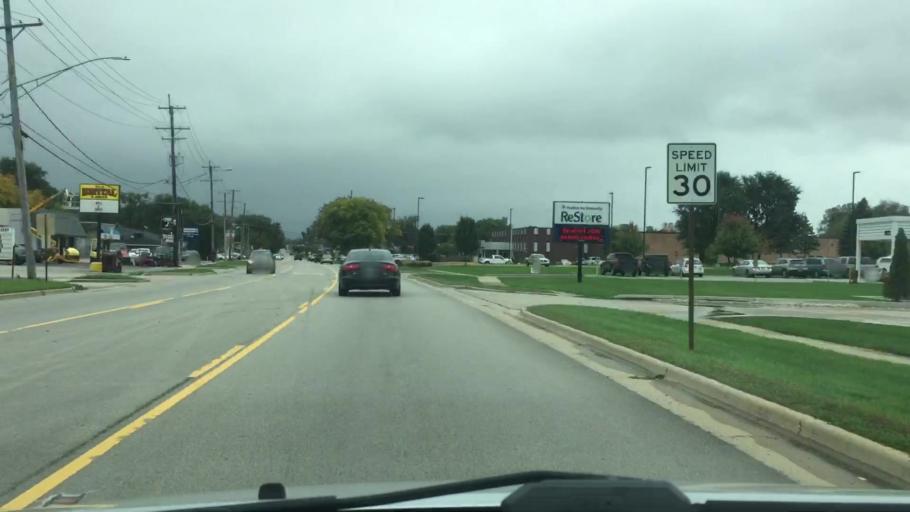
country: US
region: Illinois
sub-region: McHenry County
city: McHenry
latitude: 42.3407
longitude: -88.2746
